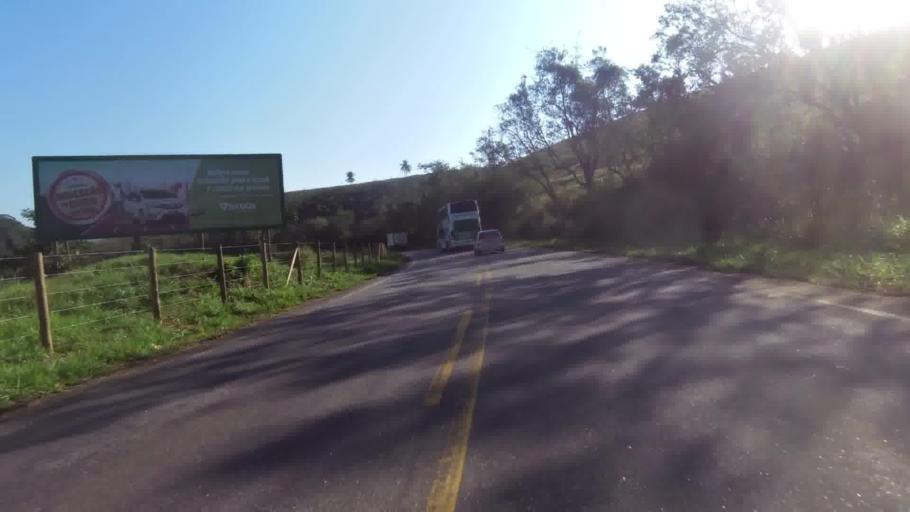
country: BR
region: Espirito Santo
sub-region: Alfredo Chaves
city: Alfredo Chaves
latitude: -20.6707
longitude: -40.7059
